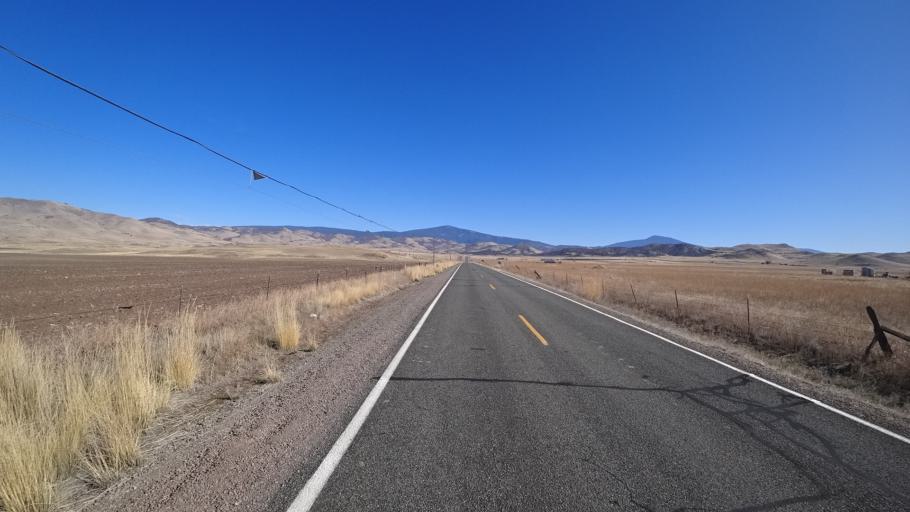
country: US
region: California
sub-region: Siskiyou County
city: Montague
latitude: 41.8082
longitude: -122.4371
